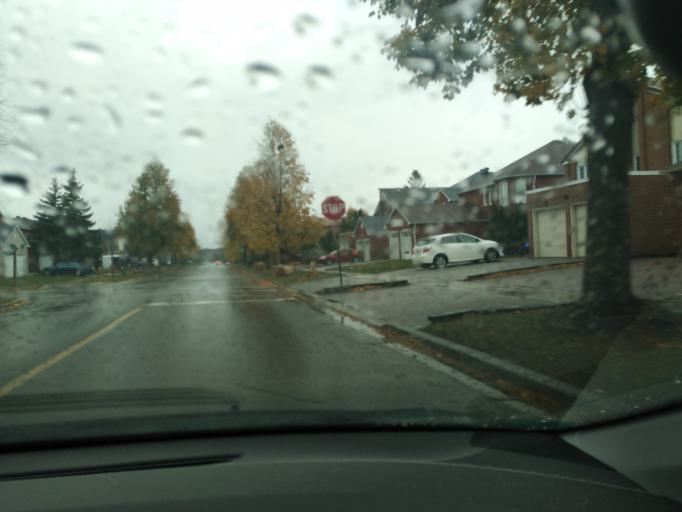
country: CA
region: Ontario
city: Markham
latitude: 43.8321
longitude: -79.2806
